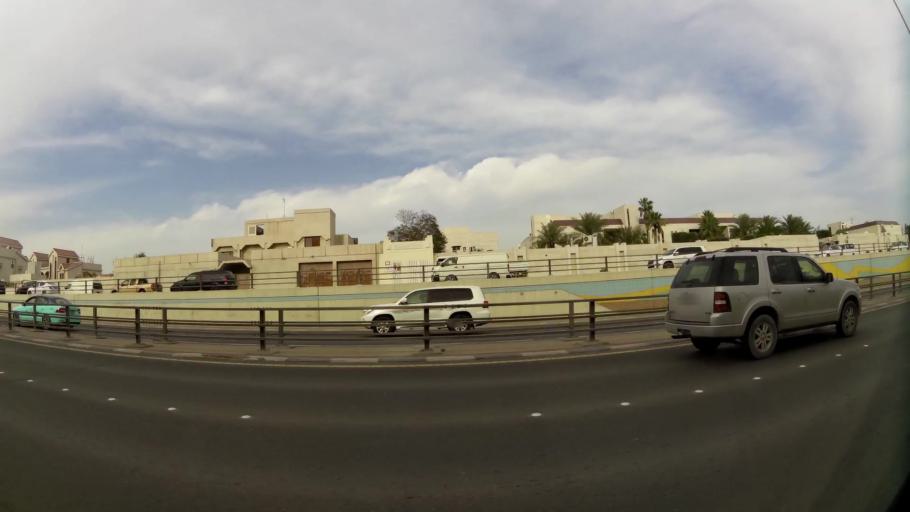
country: QA
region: Baladiyat ad Dawhah
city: Doha
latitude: 25.2665
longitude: 51.4952
